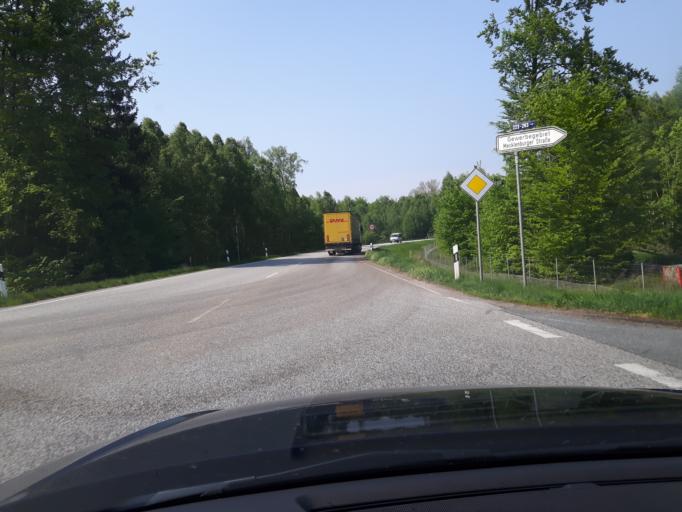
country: DE
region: Schleswig-Holstein
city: Ratekau
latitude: 53.8824
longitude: 10.7685
